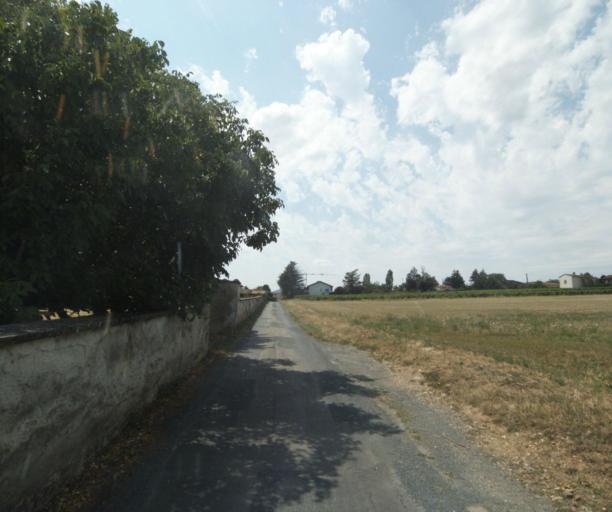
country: FR
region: Rhone-Alpes
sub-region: Departement du Rhone
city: Saint-Germain-Nuelles
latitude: 45.8435
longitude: 4.6205
